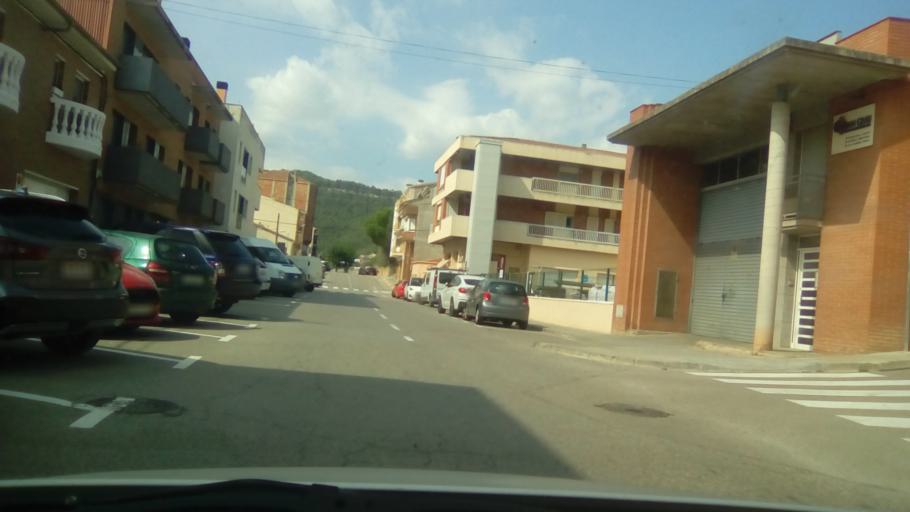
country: ES
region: Catalonia
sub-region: Provincia de Barcelona
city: Monistrol de Montserrat
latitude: 41.6291
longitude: 1.8632
